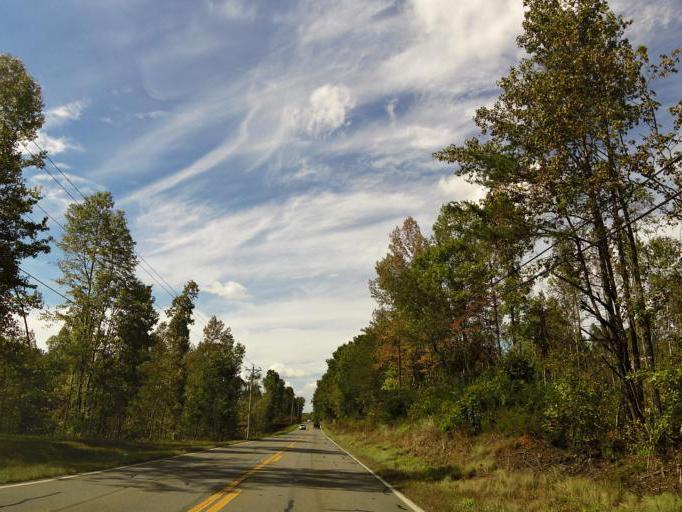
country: US
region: Georgia
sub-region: Pickens County
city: Nelson
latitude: 34.4150
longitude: -84.2974
